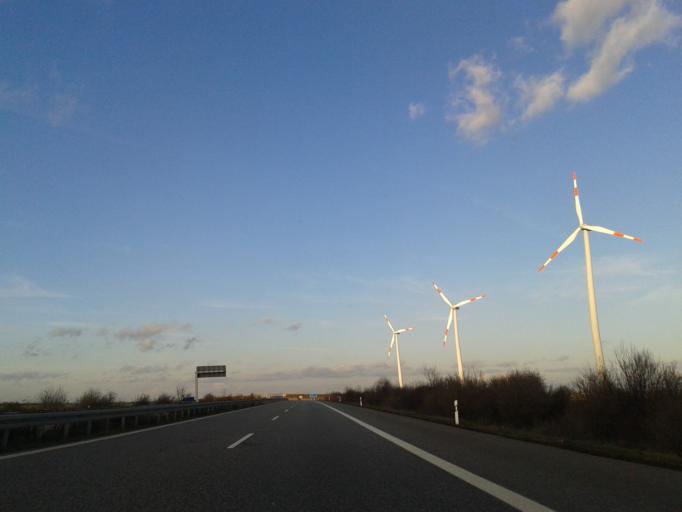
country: DE
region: Saxony-Anhalt
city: Holleben
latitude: 51.4290
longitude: 11.8646
